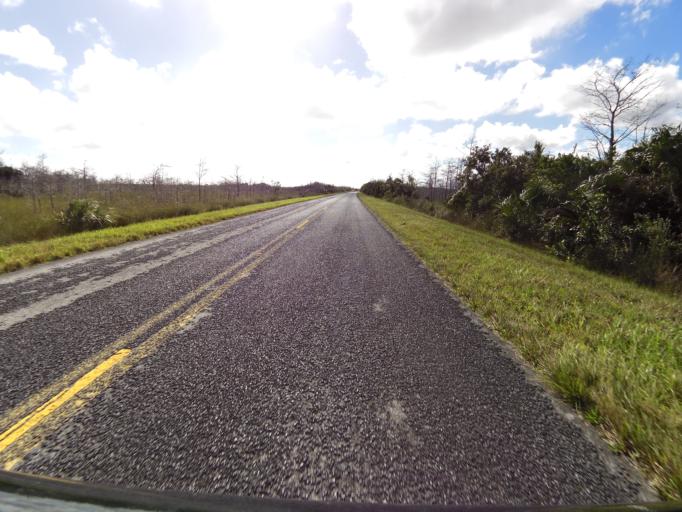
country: US
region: Florida
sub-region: Miami-Dade County
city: Florida City
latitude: 25.4100
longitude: -80.7847
